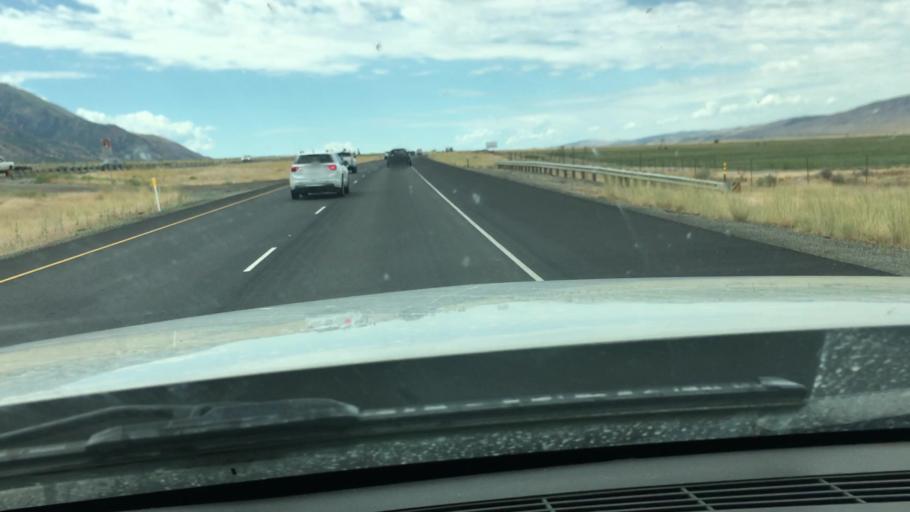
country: US
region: Utah
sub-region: Juab County
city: Mona
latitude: 39.8732
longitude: -111.8292
